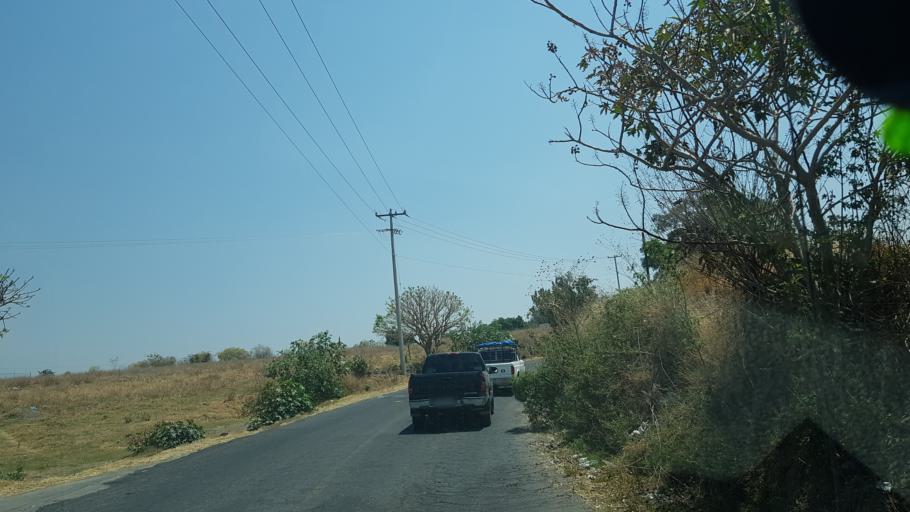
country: MX
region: Puebla
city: Tochimilco
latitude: 18.8872
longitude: -98.5484
